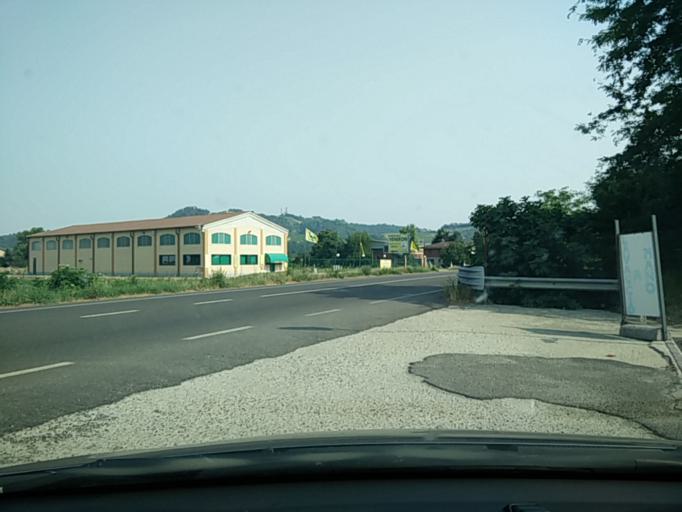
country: IT
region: Lombardy
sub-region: Provincia di Pavia
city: Broni
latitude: 45.0807
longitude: 9.2588
